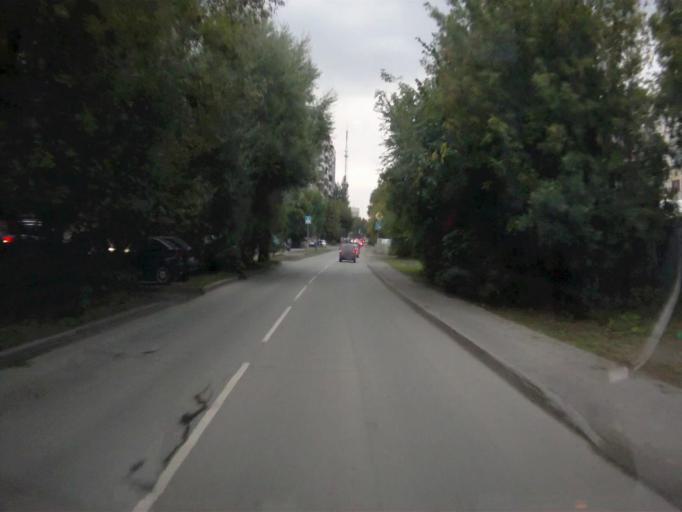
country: RU
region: Chelyabinsk
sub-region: Gorod Chelyabinsk
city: Chelyabinsk
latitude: 55.1438
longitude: 61.3962
